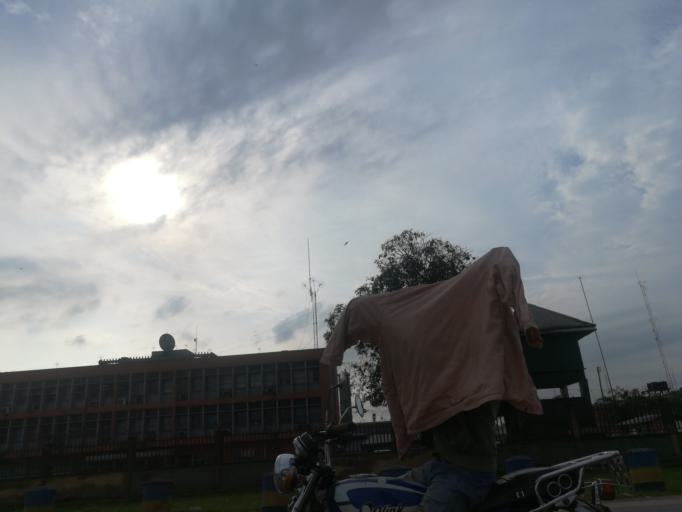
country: NG
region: Rivers
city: Okrika
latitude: 4.7659
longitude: 7.0985
